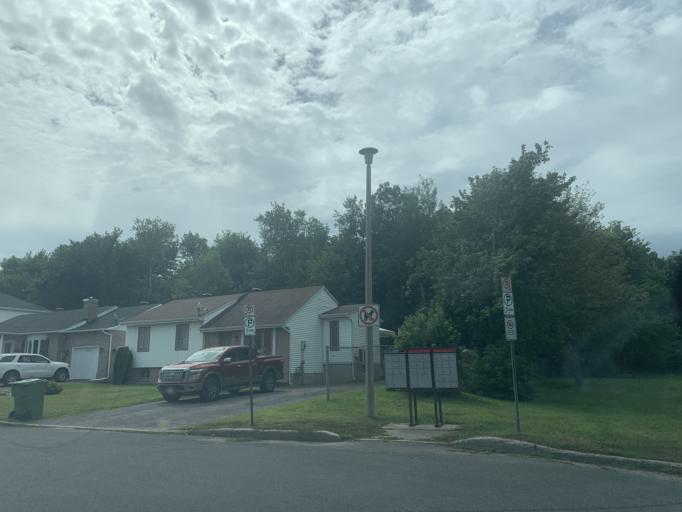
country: CA
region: Ontario
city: Hawkesbury
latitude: 45.5987
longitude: -74.6023
